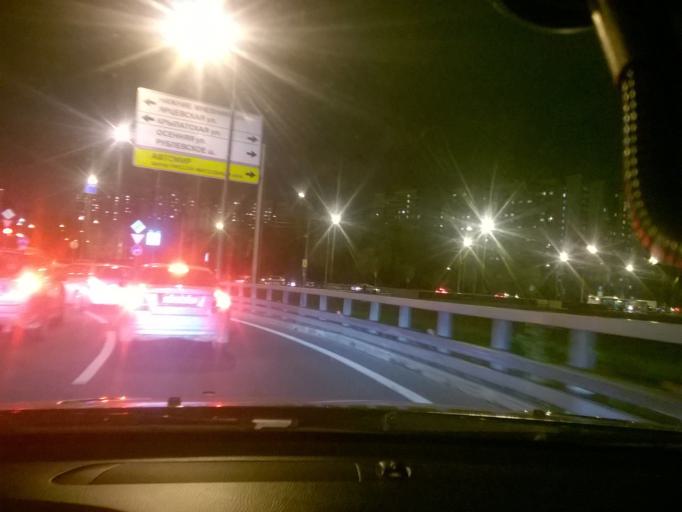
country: RU
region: Moscow
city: Shchukino
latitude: 55.7724
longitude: 37.4148
